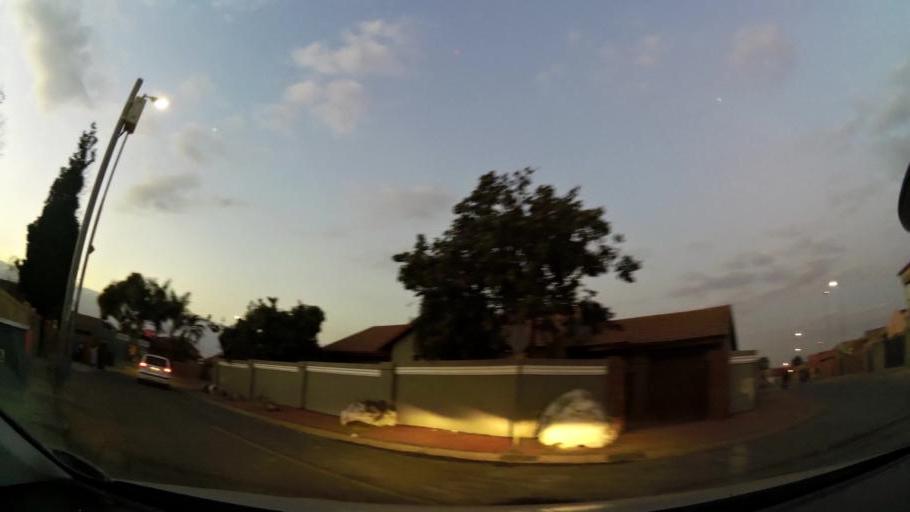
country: ZA
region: Gauteng
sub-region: City of Johannesburg Metropolitan Municipality
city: Soweto
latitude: -26.2695
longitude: 27.9034
